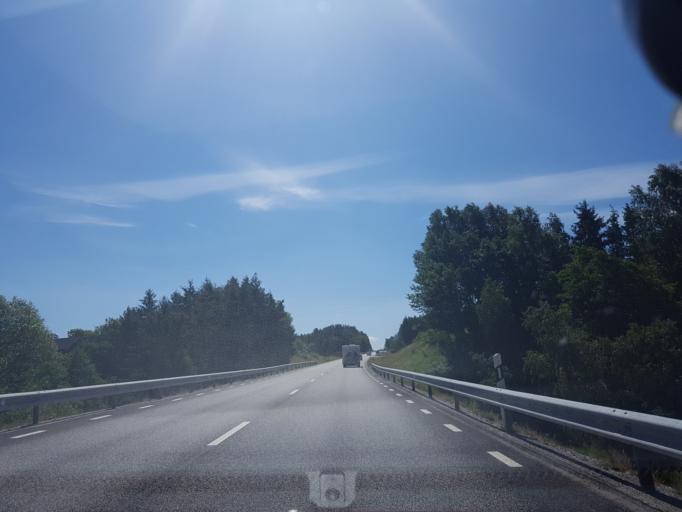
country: SE
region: Vaestra Goetaland
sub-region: Orust
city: Henan
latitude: 58.1406
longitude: 11.6446
